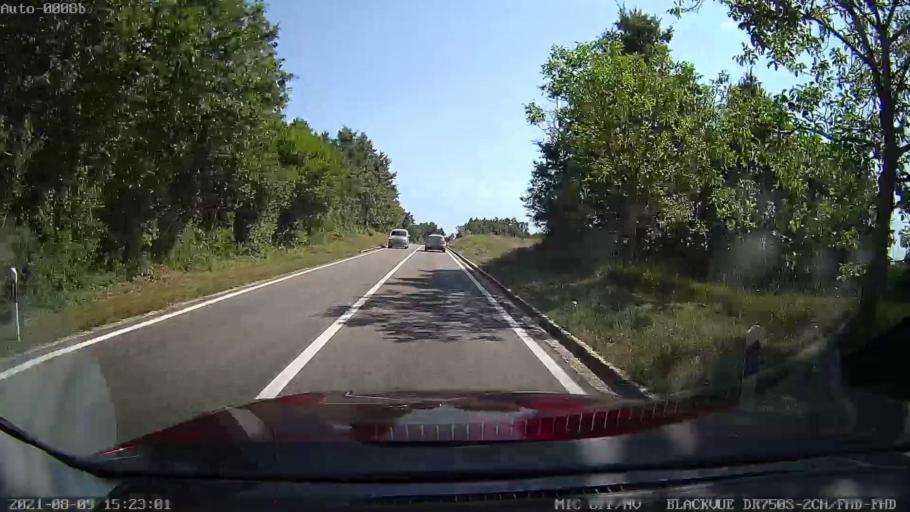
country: HR
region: Istarska
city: Pazin
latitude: 45.1862
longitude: 13.9028
